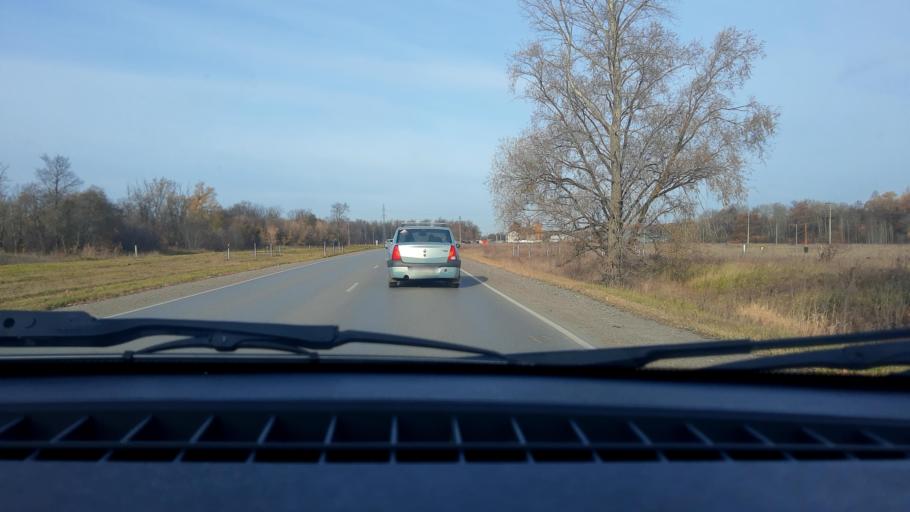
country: RU
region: Bashkortostan
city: Mikhaylovka
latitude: 54.8021
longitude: 55.8318
